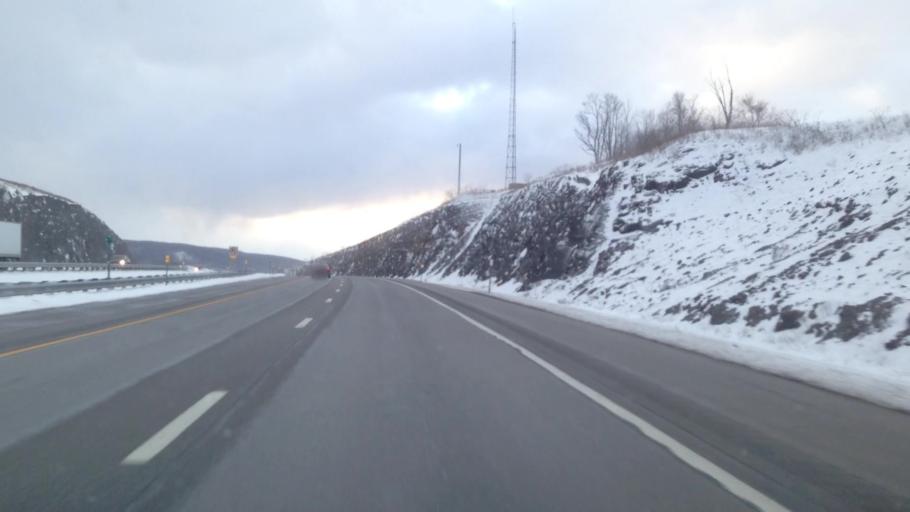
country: US
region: New York
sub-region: Herkimer County
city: Little Falls
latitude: 43.0118
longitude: -74.8556
